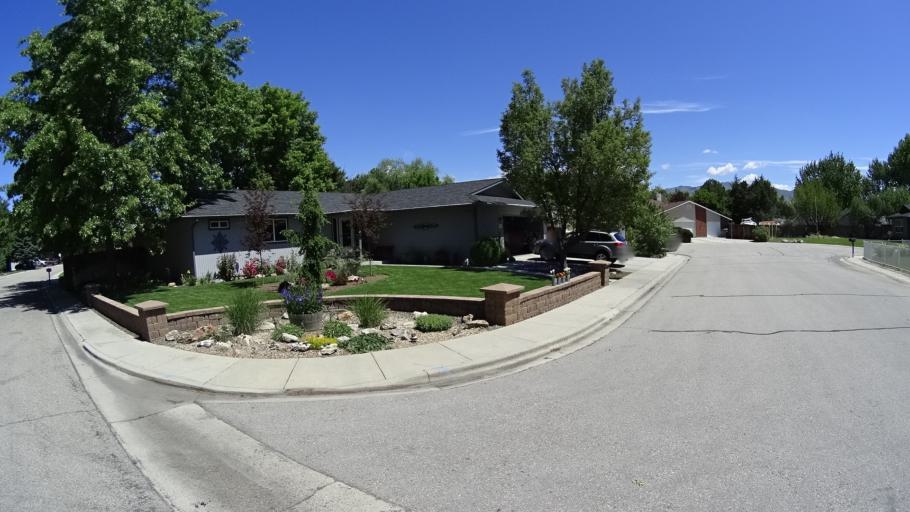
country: US
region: Idaho
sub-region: Ada County
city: Boise
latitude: 43.5690
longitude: -116.1692
